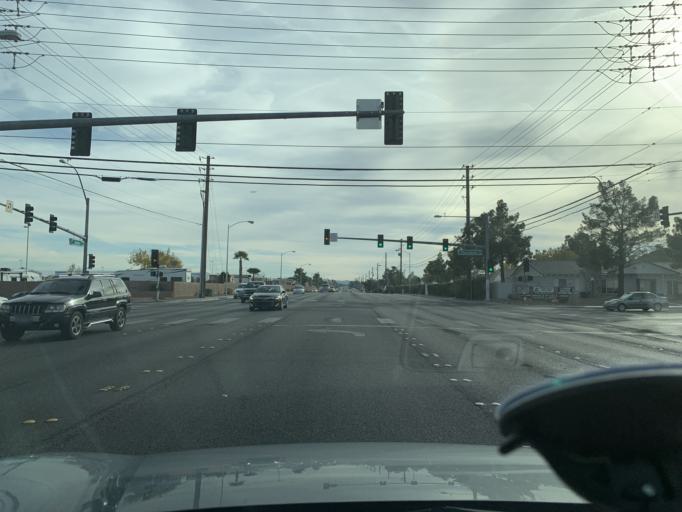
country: US
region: Nevada
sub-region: Clark County
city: Spring Valley
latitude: 36.1075
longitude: -115.2250
